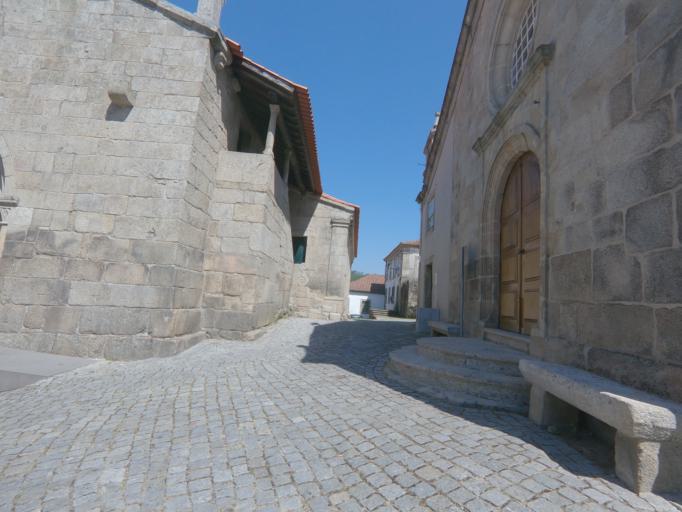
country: PT
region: Viseu
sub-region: Tarouca
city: Tarouca
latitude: 41.0166
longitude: -7.7751
